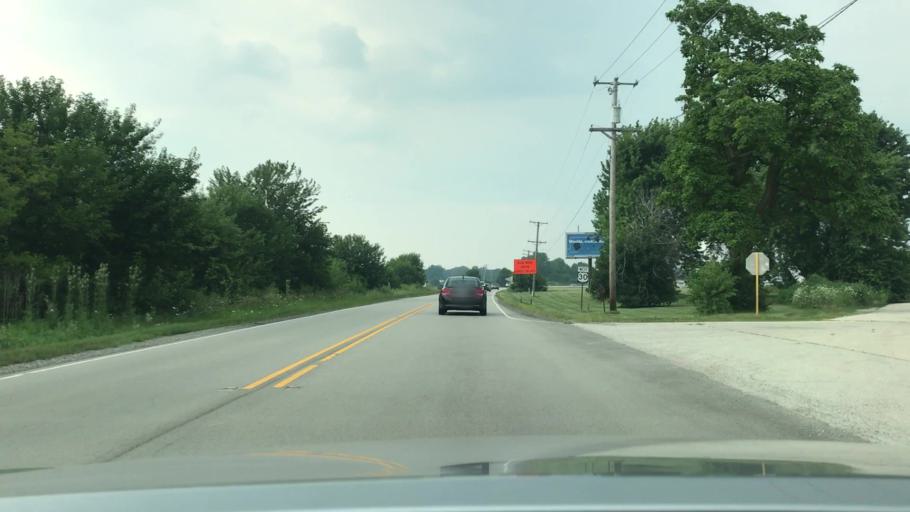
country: US
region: Illinois
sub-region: Will County
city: Plainfield
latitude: 41.6546
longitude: -88.2328
